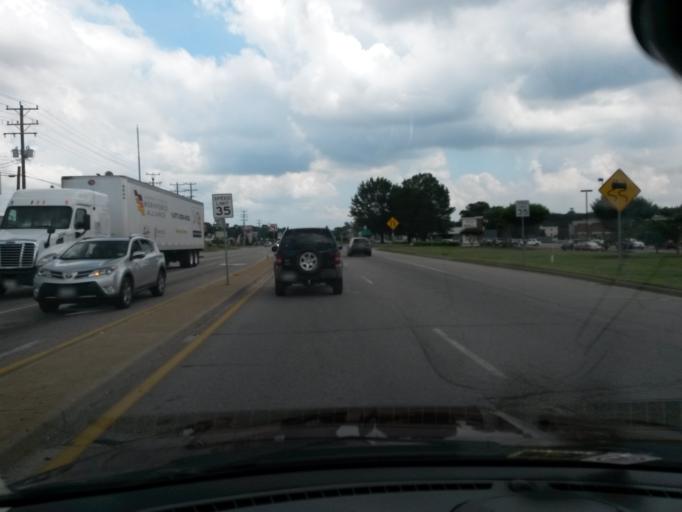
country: US
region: Virginia
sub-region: Chesterfield County
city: Chester
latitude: 37.3550
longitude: -77.4125
